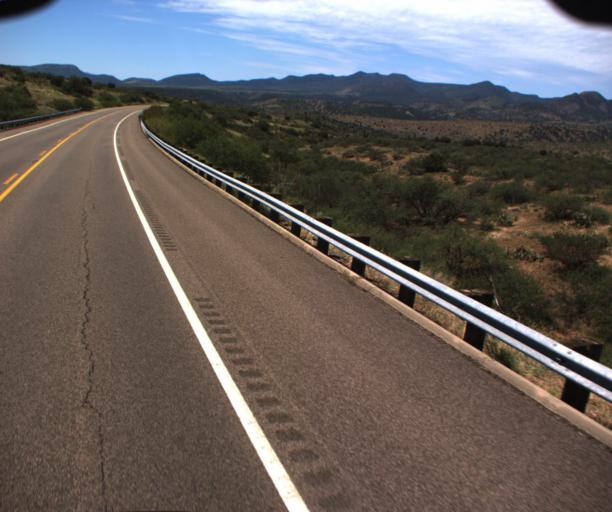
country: US
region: Arizona
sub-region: Gila County
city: Globe
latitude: 33.6020
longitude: -110.6328
